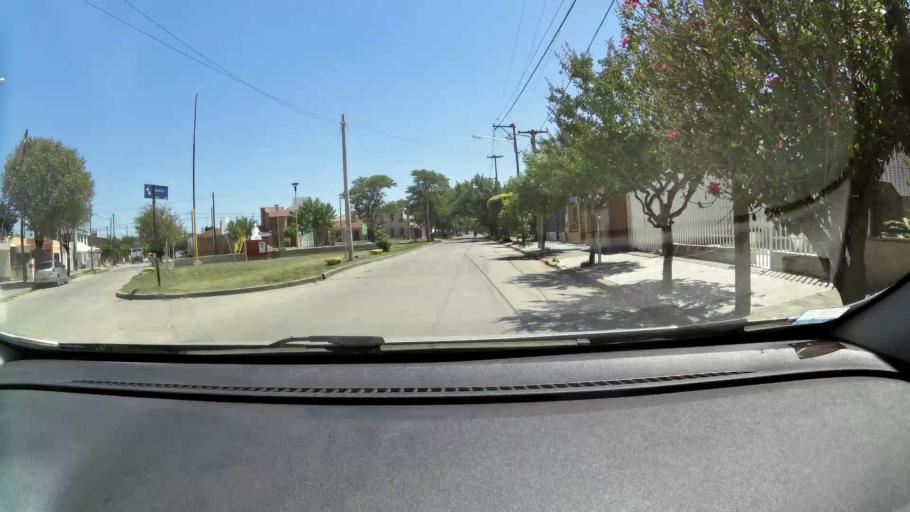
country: AR
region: Cordoba
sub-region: Departamento de Capital
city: Cordoba
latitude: -31.4330
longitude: -64.1272
